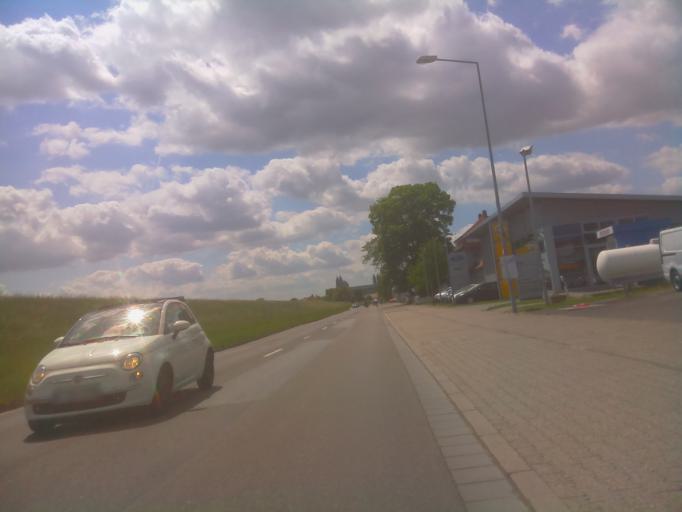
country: DE
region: Rheinland-Pfalz
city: Speyer
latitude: 49.3302
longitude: 8.4510
